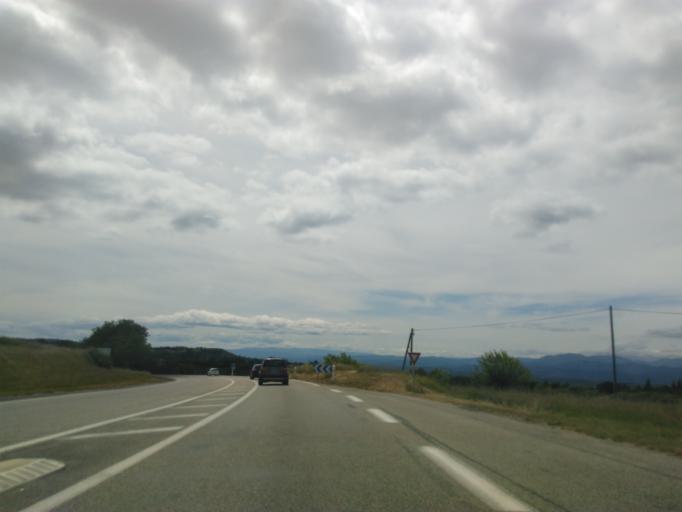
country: FR
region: Rhone-Alpes
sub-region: Departement de l'Ardeche
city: Villeneuve-de-Berg
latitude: 44.5773
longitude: 4.5227
